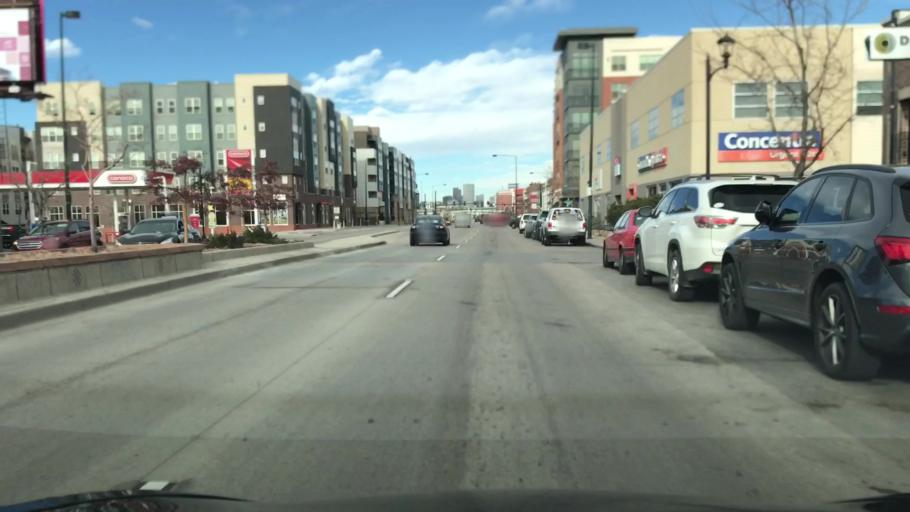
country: US
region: Colorado
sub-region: Denver County
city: Denver
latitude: 39.6939
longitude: -104.9874
